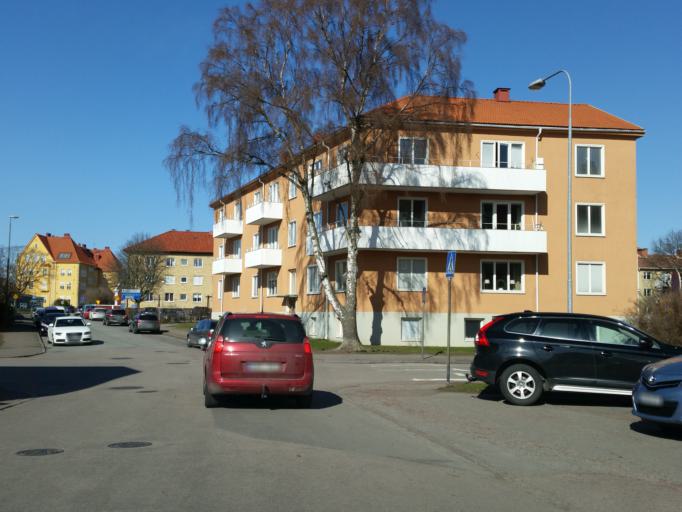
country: SE
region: Kalmar
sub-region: Kalmar Kommun
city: Kalmar
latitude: 56.6609
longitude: 16.3478
